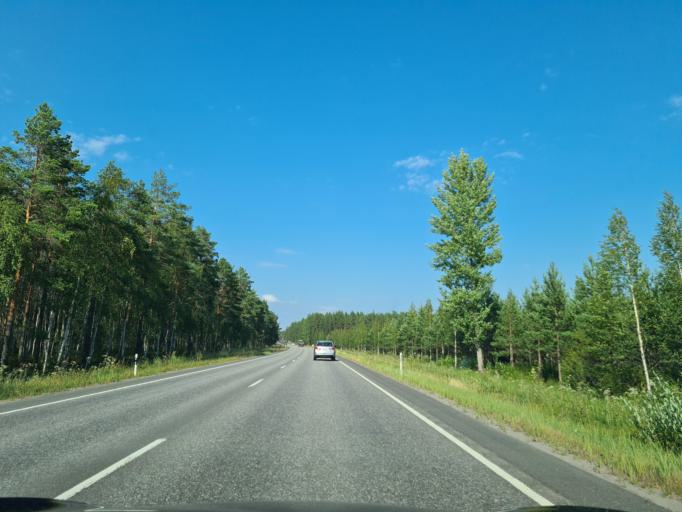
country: FI
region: Satakunta
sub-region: Pohjois-Satakunta
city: Kankaanpaeae
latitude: 61.8416
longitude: 22.4495
